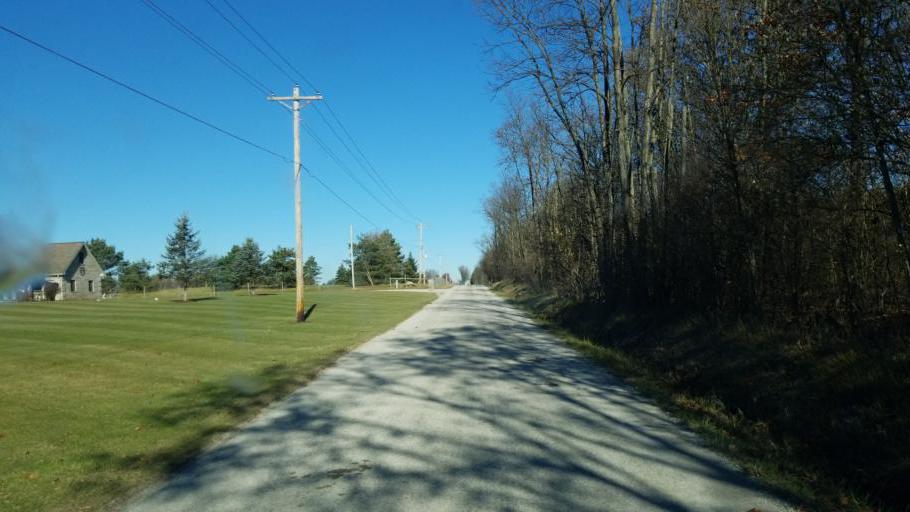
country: US
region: Ohio
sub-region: Ashland County
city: Ashland
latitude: 40.8589
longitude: -82.3878
